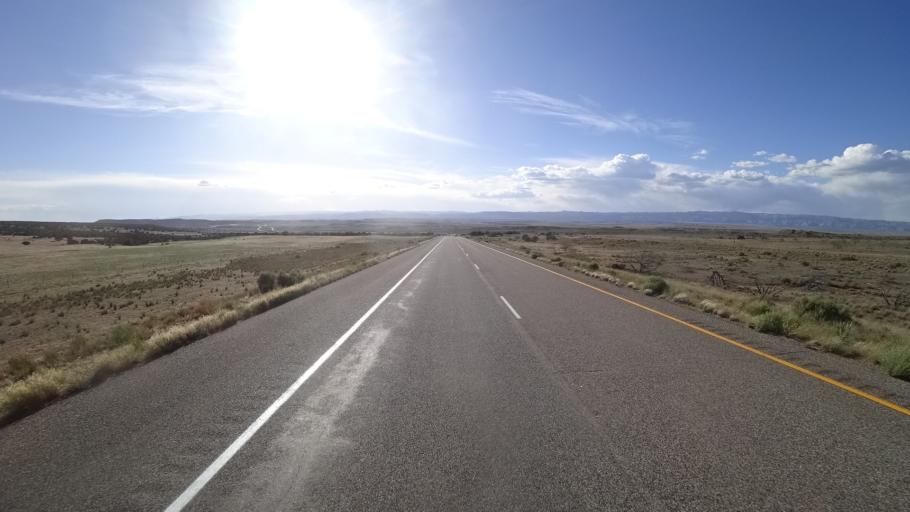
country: US
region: Colorado
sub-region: Mesa County
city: Loma
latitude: 39.1908
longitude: -109.0446
